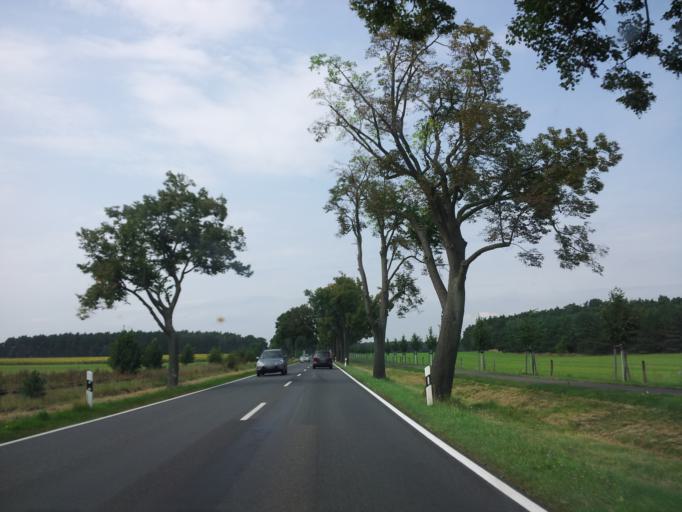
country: DE
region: Brandenburg
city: Belzig
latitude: 52.1174
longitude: 12.6435
